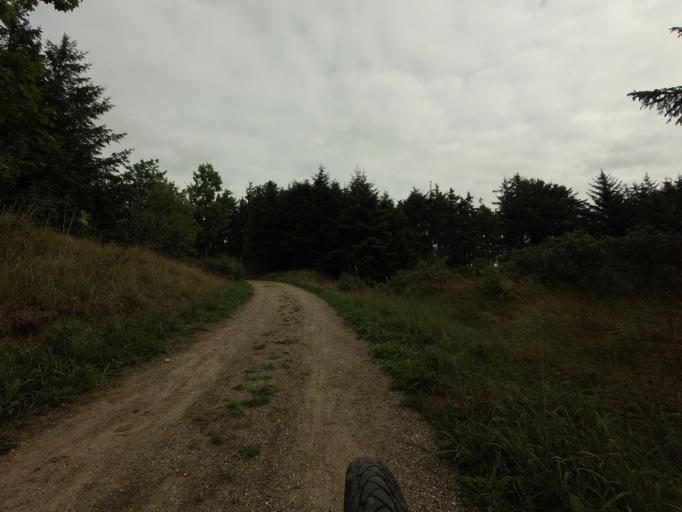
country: DK
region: North Denmark
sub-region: Hjorring Kommune
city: Hirtshals
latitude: 57.5495
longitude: 9.9193
